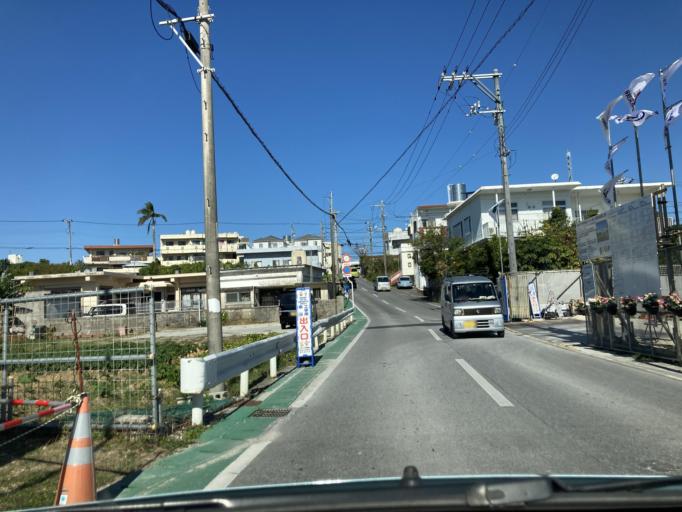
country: JP
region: Okinawa
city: Okinawa
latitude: 26.3570
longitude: 127.8247
